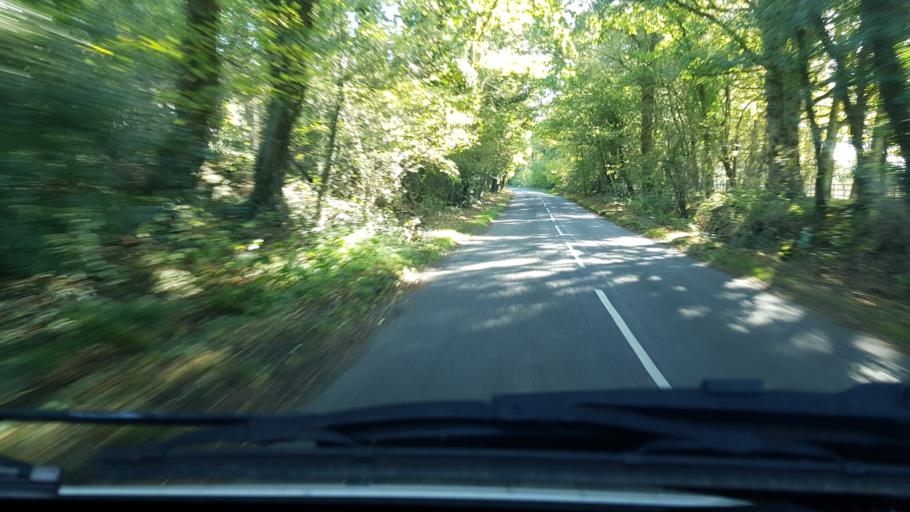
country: GB
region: England
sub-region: West Sussex
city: Rudgwick
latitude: 51.1364
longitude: -0.4269
